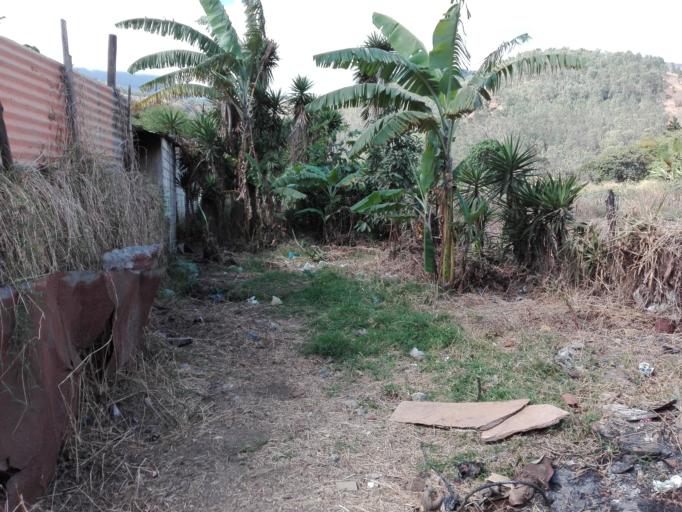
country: GT
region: Guatemala
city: Villa Canales
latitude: 14.4268
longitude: -90.5526
